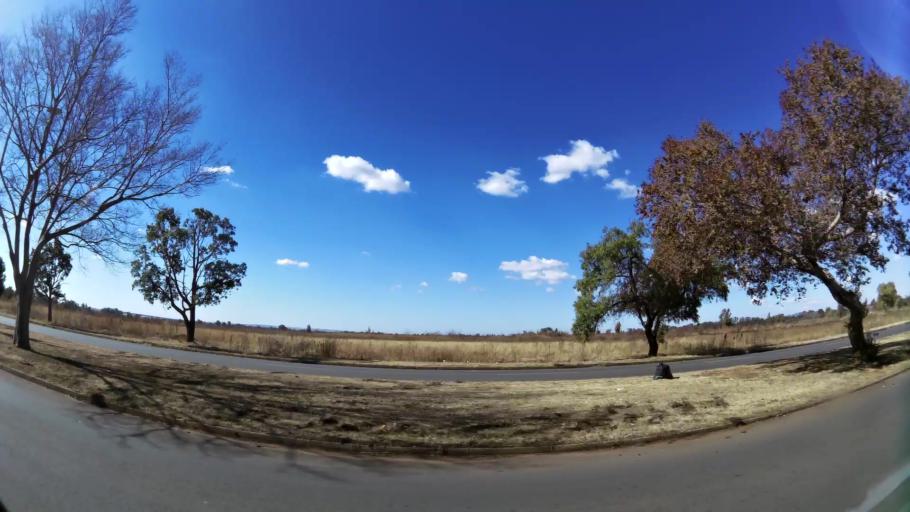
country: ZA
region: Gauteng
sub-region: West Rand District Municipality
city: Carletonville
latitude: -26.3478
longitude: 27.3965
